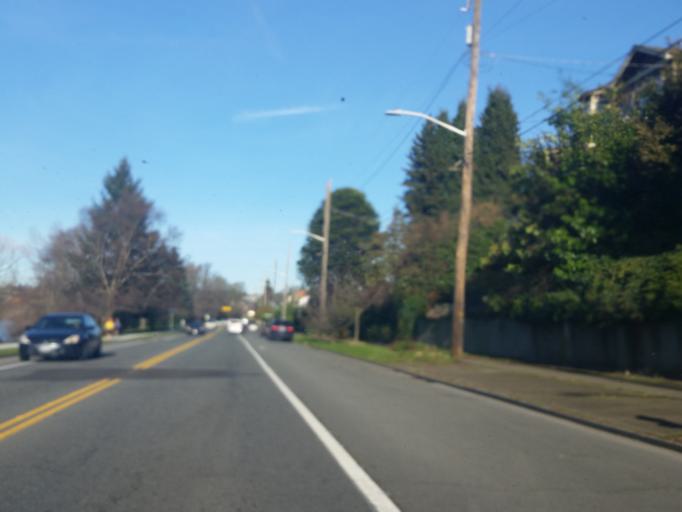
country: US
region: Washington
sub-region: King County
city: Seattle
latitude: 47.6728
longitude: -122.3366
